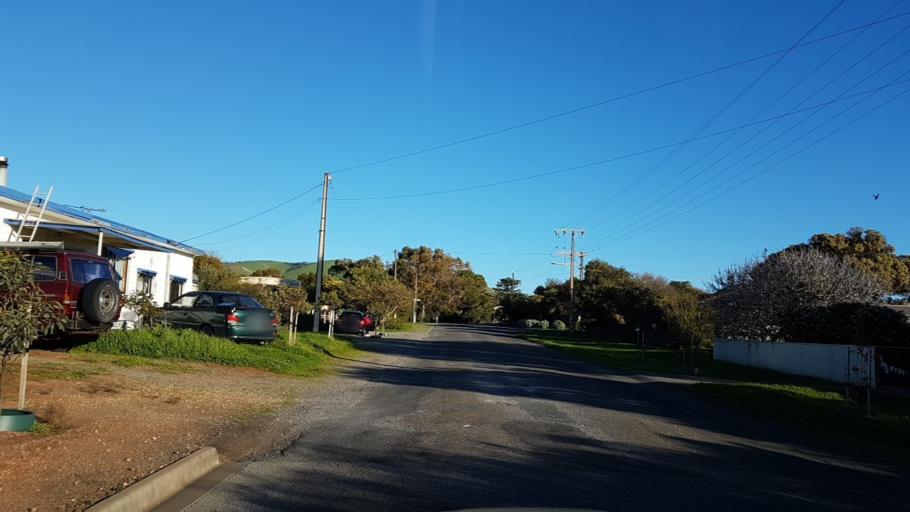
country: AU
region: South Australia
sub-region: Onkaparinga
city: Port Willunga
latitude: -35.3332
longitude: 138.4505
